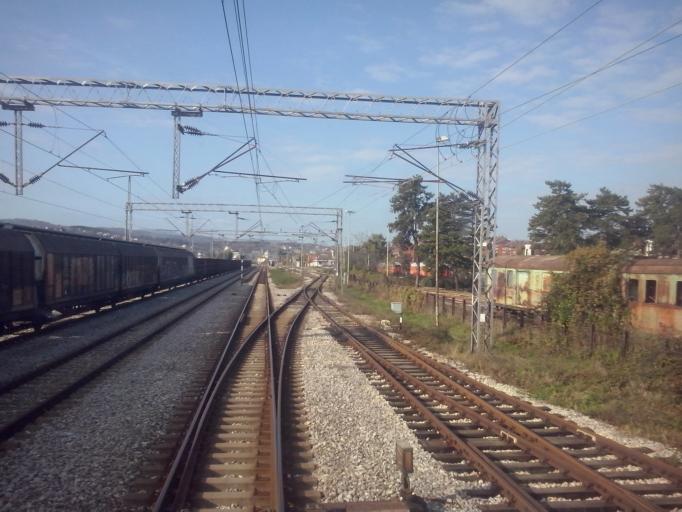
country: RS
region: Central Serbia
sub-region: Kolubarski Okrug
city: Valjevo
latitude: 44.2712
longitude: 19.9121
